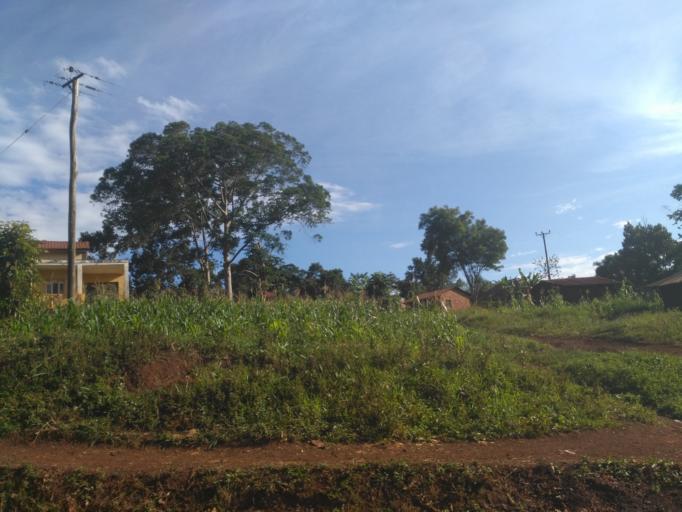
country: UG
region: Eastern Region
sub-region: Jinja District
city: Jinja
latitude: 0.4644
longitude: 33.1804
